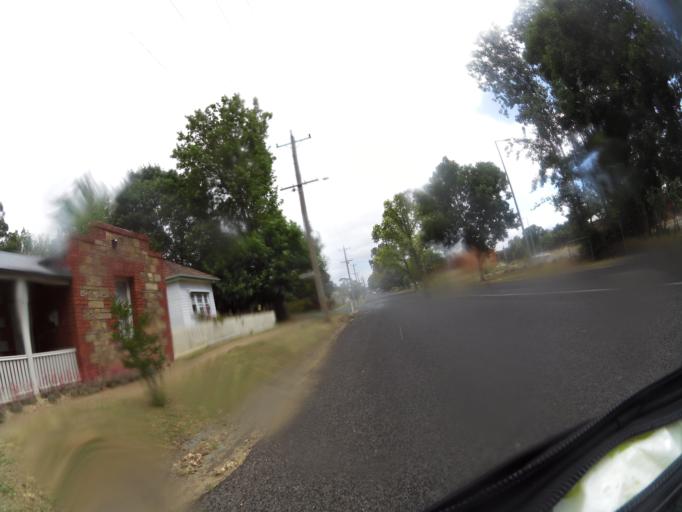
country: AU
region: Victoria
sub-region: Mount Alexander
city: Castlemaine
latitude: -37.0602
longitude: 144.2150
